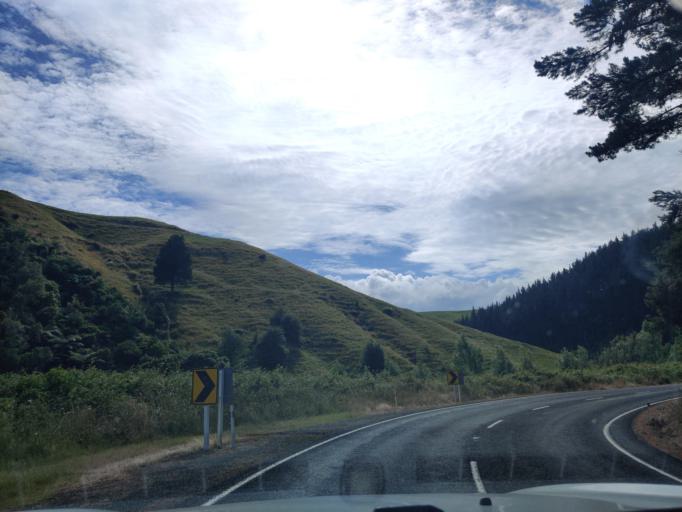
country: NZ
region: Waikato
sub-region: Otorohanga District
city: Otorohanga
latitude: -38.0966
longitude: 175.1253
